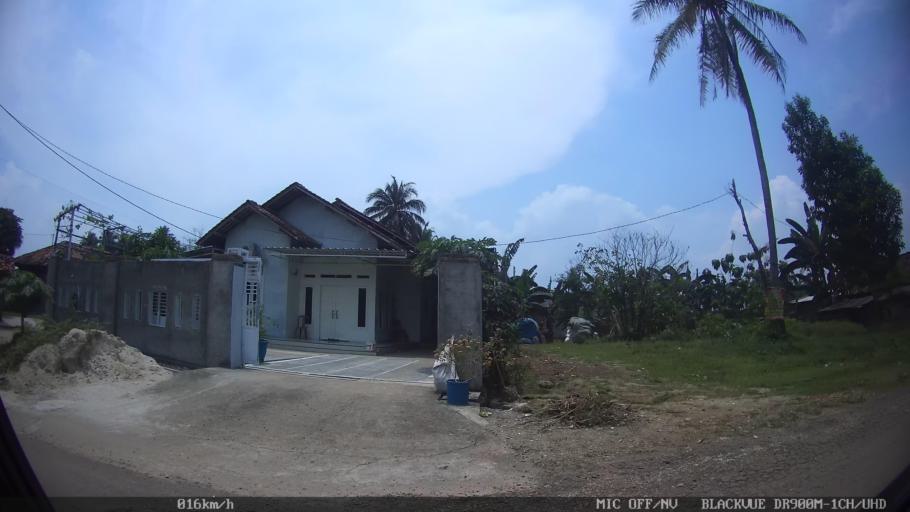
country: ID
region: Lampung
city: Natar
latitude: -5.3143
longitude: 105.2322
